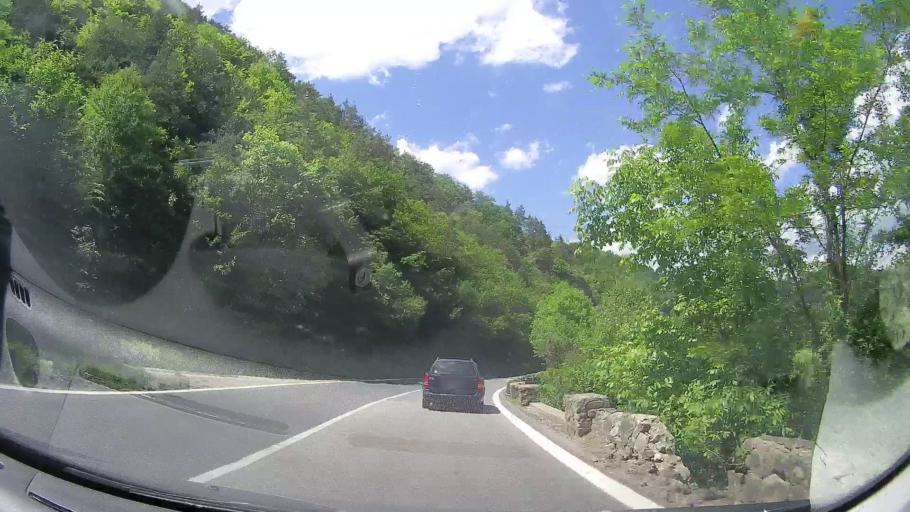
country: RO
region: Valcea
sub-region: Comuna Brezoi
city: Brezoi
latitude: 45.3600
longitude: 24.2941
